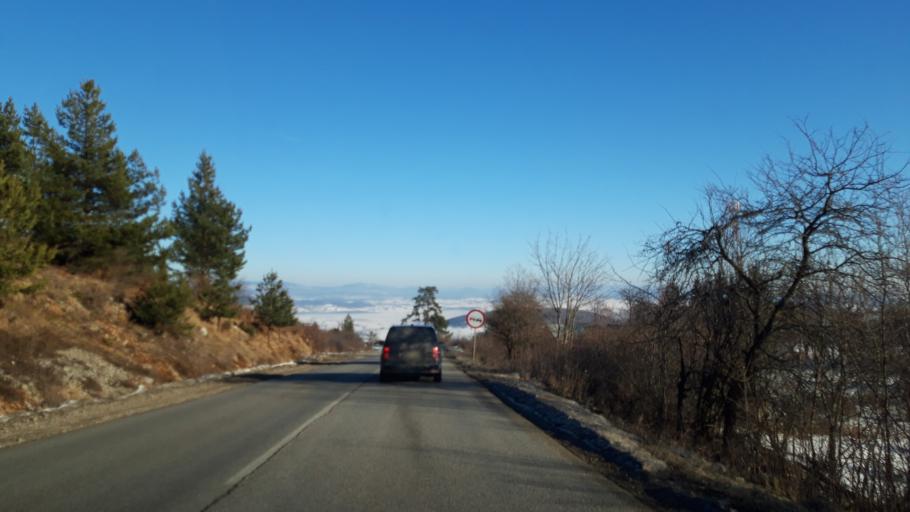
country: BA
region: Republika Srpska
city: Sokolac
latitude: 43.9163
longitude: 18.7288
